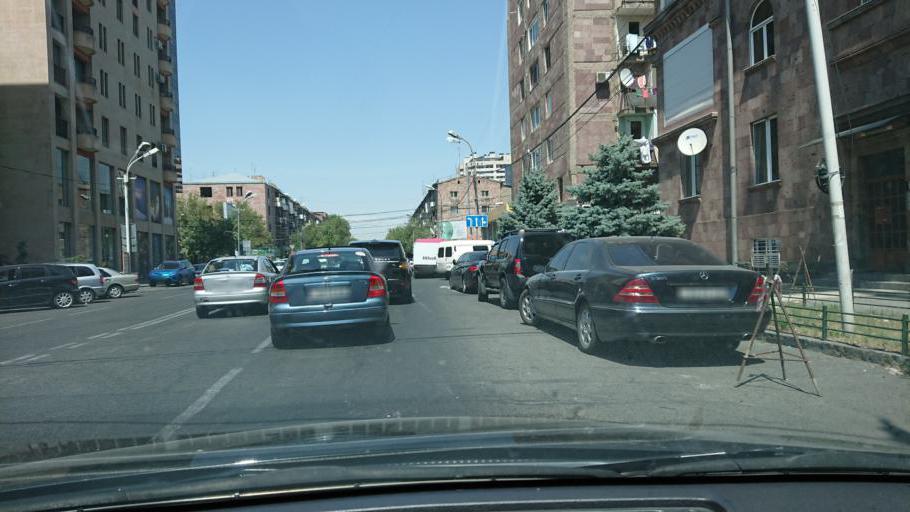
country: AM
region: Yerevan
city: Yerevan
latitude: 40.2000
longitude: 44.5007
